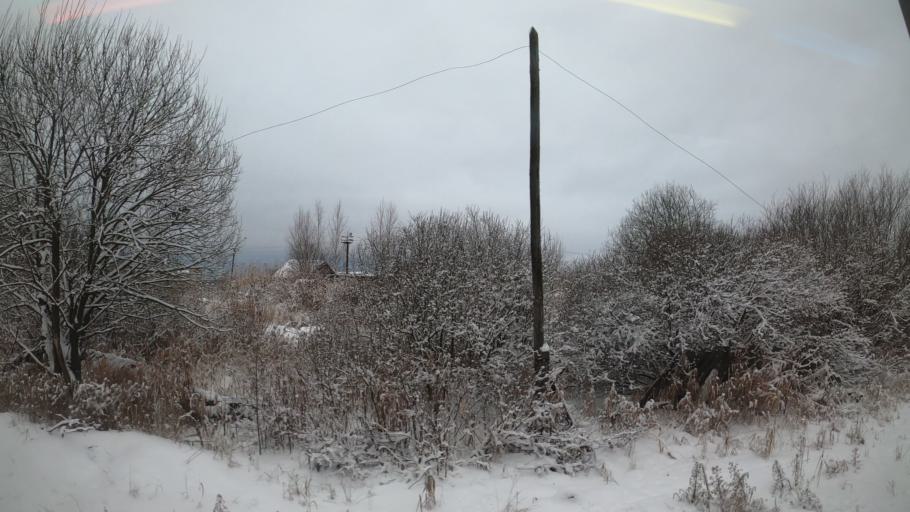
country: RU
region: Jaroslavl
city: Pereslavl'-Zalesskiy
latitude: 56.7338
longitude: 38.8950
